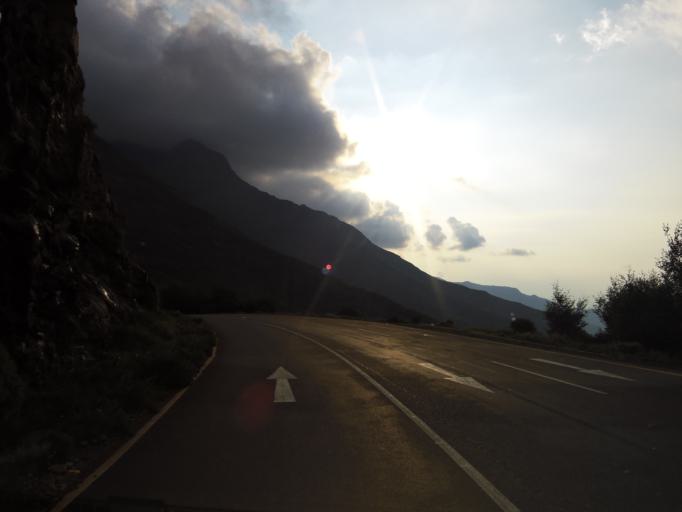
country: LS
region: Butha-Buthe
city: Butha-Buthe
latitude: -29.0612
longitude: 28.3661
